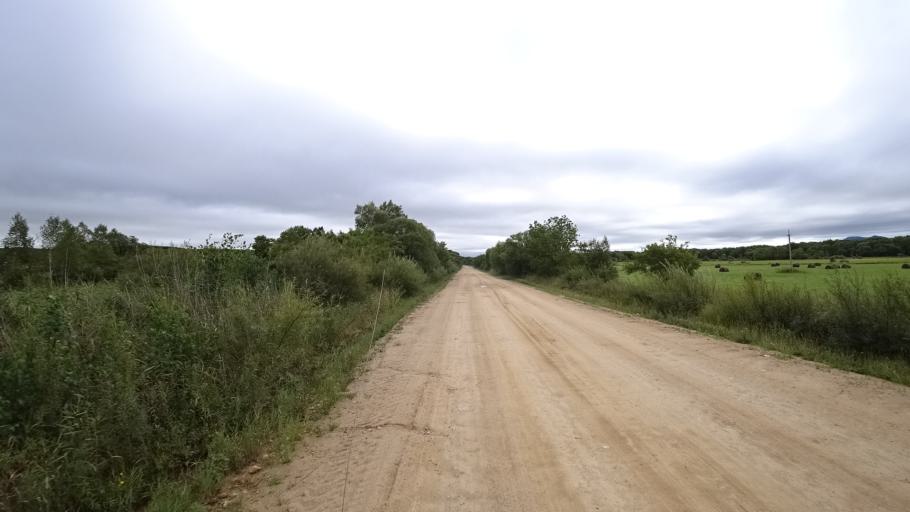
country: RU
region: Primorskiy
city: Monastyrishche
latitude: 44.1038
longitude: 132.6096
